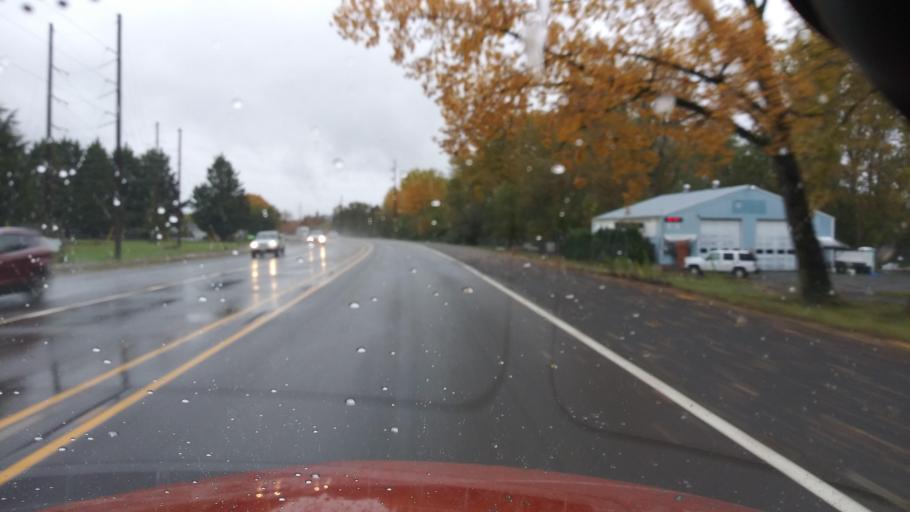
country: US
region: Oregon
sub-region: Washington County
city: Forest Grove
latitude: 45.5090
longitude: -123.1022
